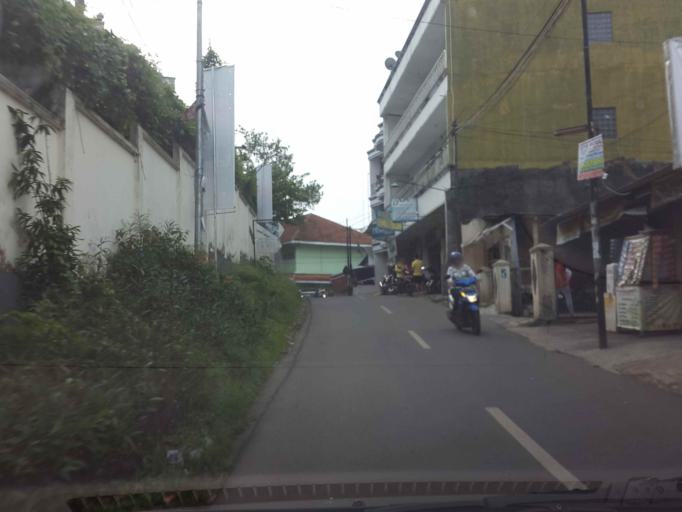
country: ID
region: Central Java
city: Salatiga
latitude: -7.3176
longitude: 110.4986
